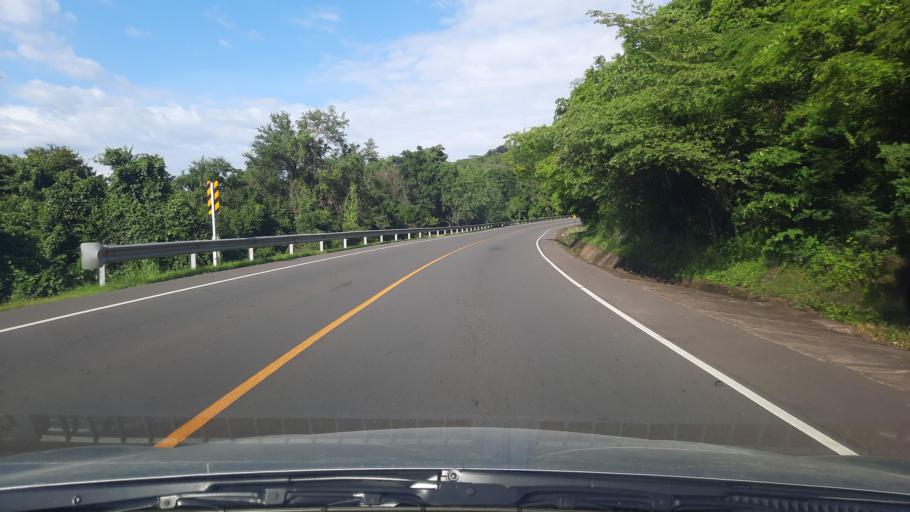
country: NI
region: Leon
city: Telica
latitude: 12.6904
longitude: -86.8541
